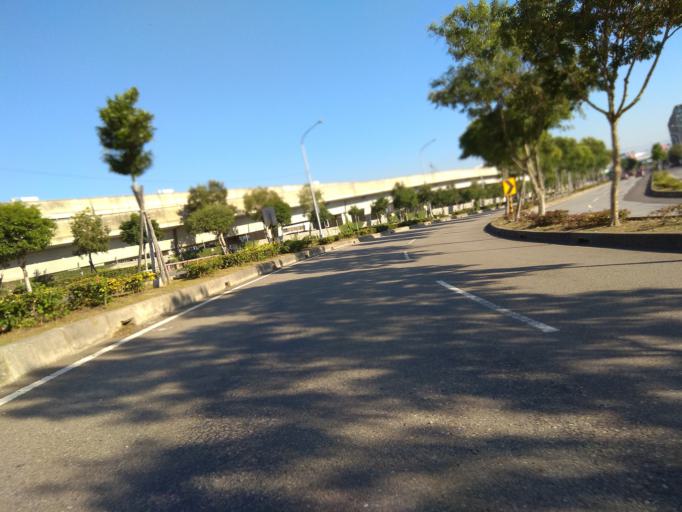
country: TW
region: Taiwan
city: Taoyuan City
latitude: 25.0255
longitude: 121.2188
